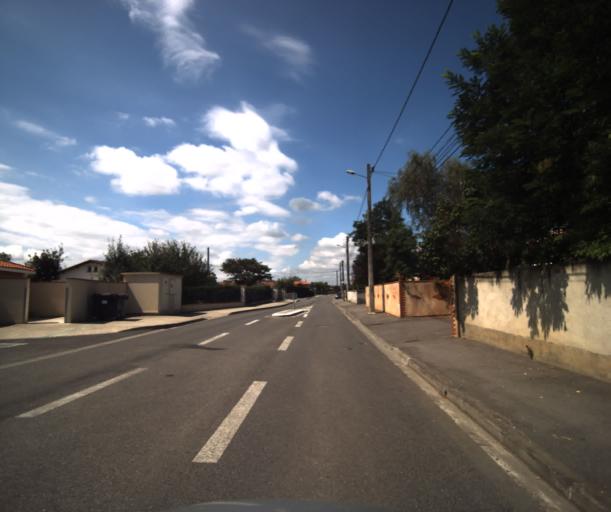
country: FR
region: Midi-Pyrenees
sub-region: Departement de la Haute-Garonne
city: Lacasse
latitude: 43.3922
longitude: 1.2562
